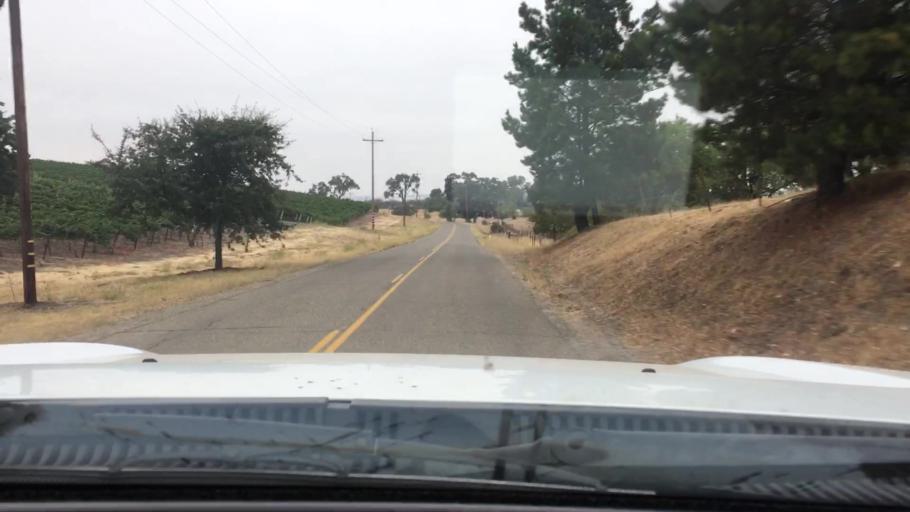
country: US
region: California
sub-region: San Luis Obispo County
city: Atascadero
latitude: 35.5447
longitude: -120.6097
